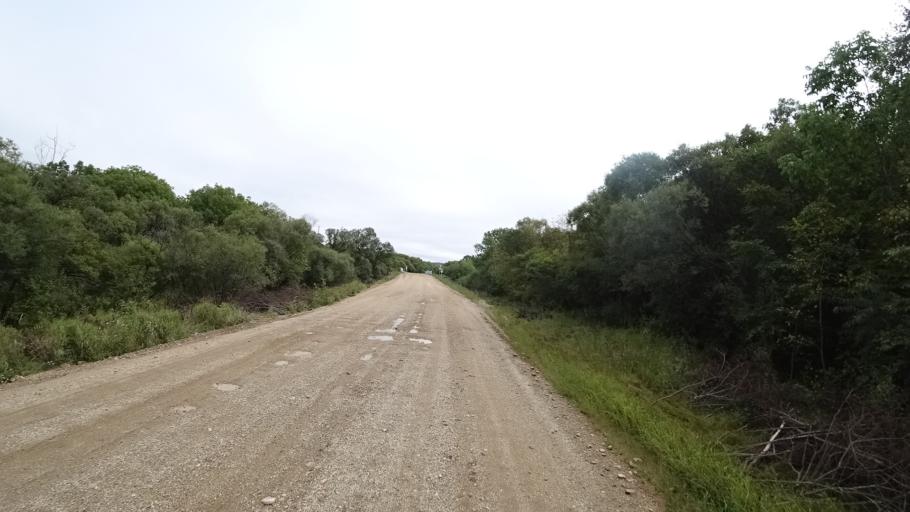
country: RU
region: Primorskiy
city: Lyalichi
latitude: 44.0829
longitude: 132.4466
